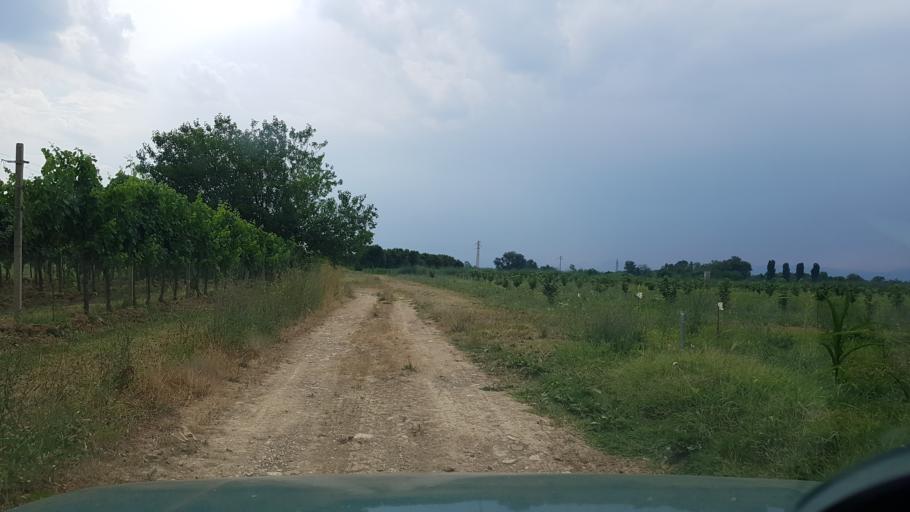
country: IT
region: Friuli Venezia Giulia
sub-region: Provincia di Udine
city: Faedis
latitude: 46.1339
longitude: 13.3249
